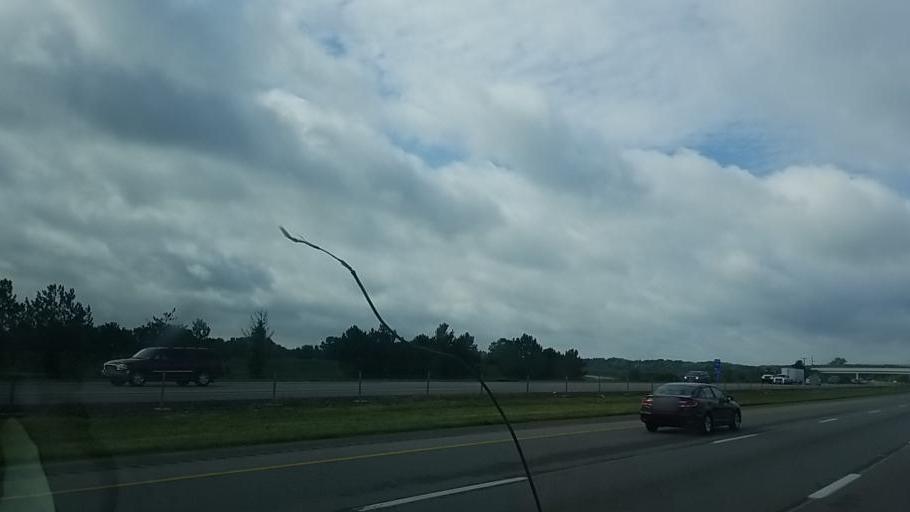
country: US
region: Ohio
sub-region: Delaware County
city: Sunbury
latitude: 40.3164
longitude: -82.9112
